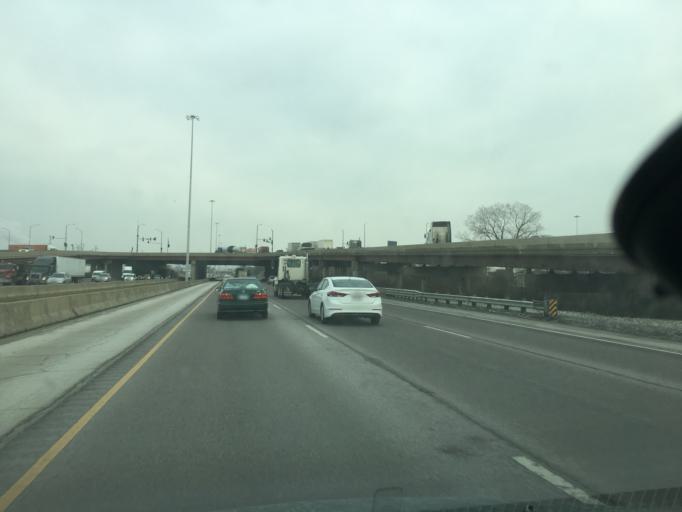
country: US
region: Illinois
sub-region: Cook County
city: Cicero
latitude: 41.8222
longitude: -87.7269
